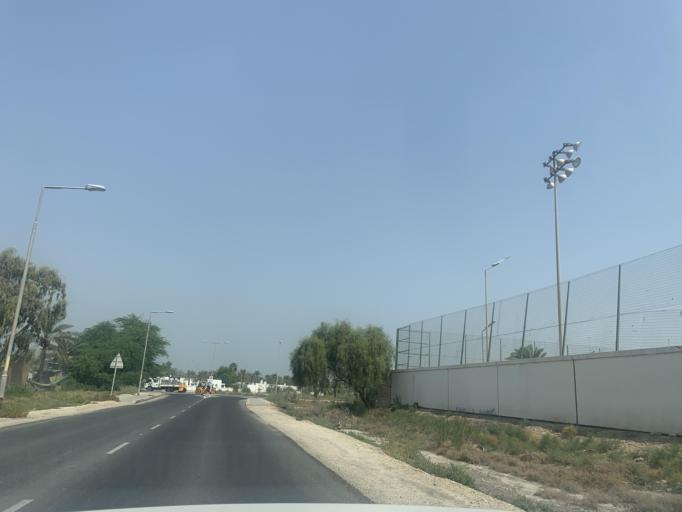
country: BH
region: Central Governorate
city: Madinat Hamad
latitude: 26.1569
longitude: 50.4680
